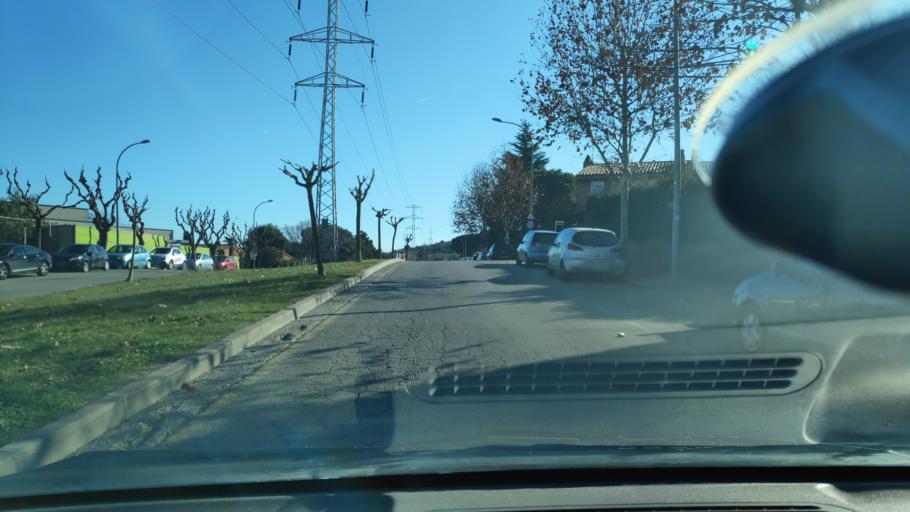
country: ES
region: Catalonia
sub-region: Provincia de Barcelona
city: Sant Quirze del Valles
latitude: 41.5298
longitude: 2.0753
